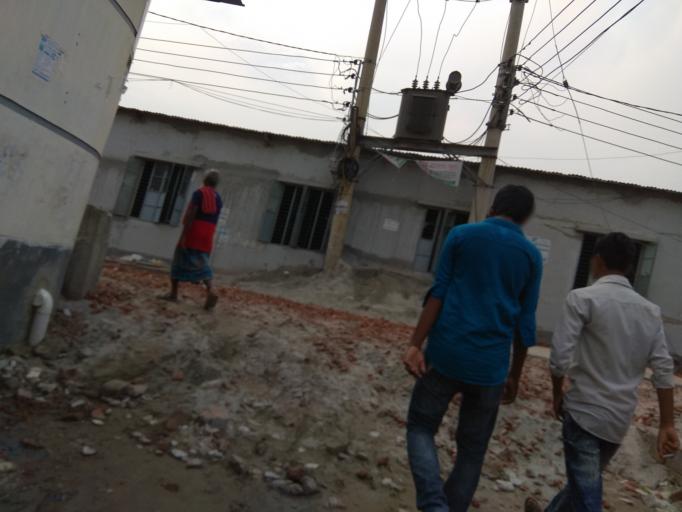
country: BD
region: Dhaka
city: Tungi
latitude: 23.8149
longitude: 90.3829
